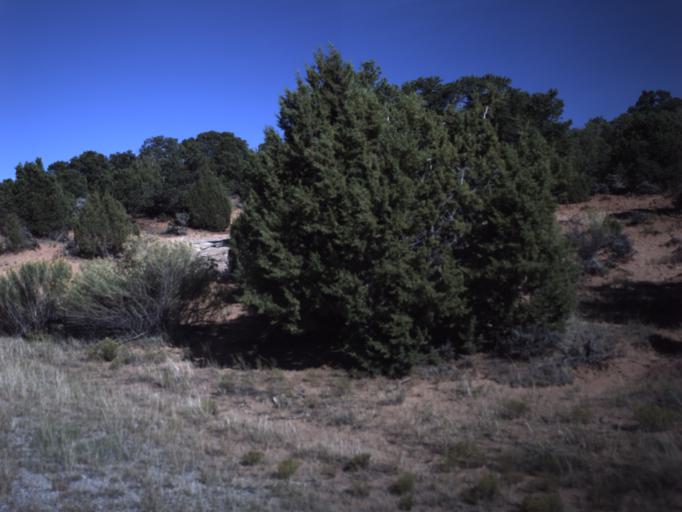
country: US
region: Utah
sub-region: San Juan County
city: Monticello
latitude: 37.9924
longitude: -109.4884
